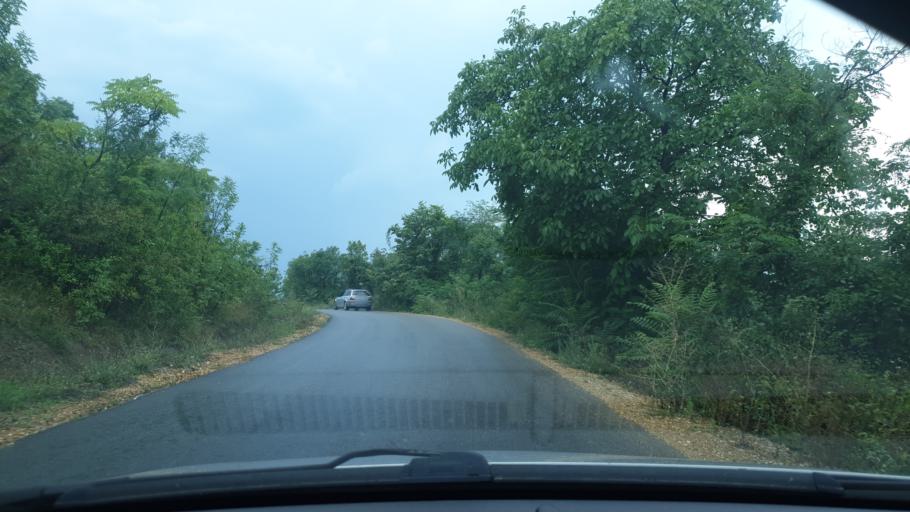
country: RS
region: Central Serbia
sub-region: Sumadijski Okrug
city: Kragujevac
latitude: 44.0664
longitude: 20.7916
